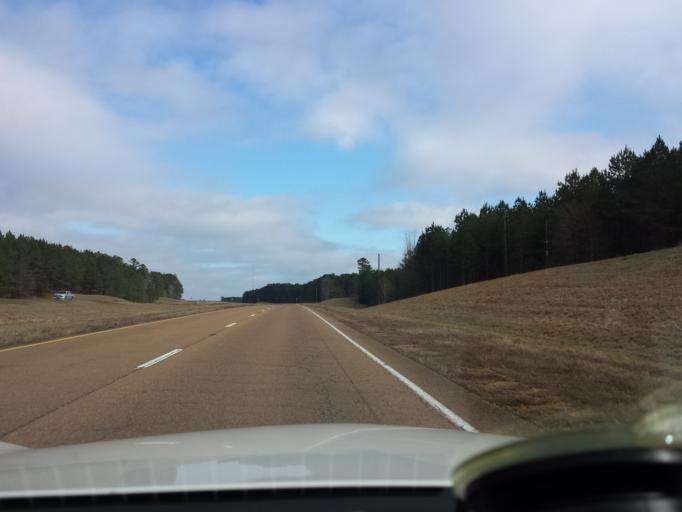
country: US
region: Mississippi
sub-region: Neshoba County
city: Pearl River
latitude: 32.9024
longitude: -89.3437
